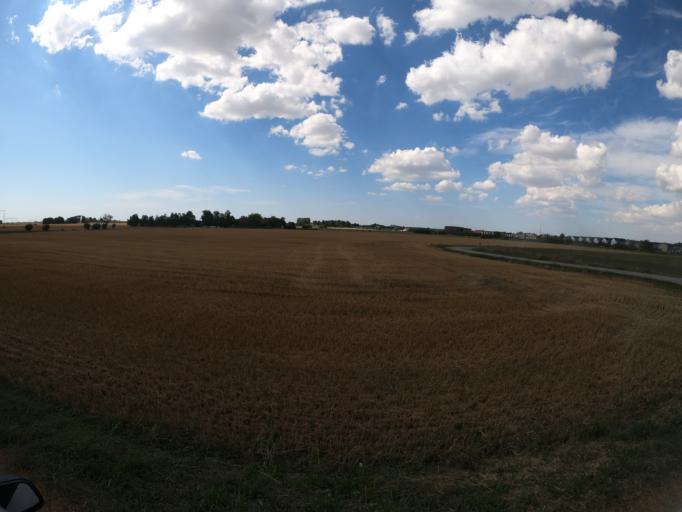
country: SE
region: Skane
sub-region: Lunds Kommun
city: Lund
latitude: 55.6878
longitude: 13.2424
